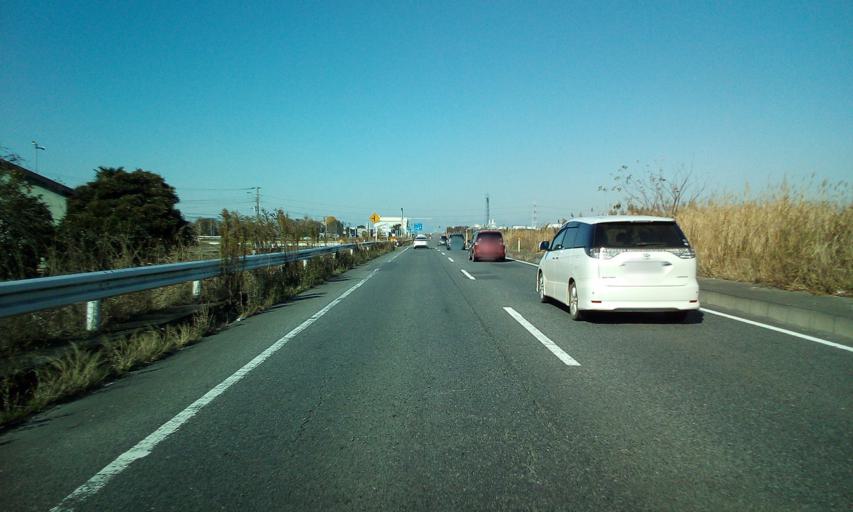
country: JP
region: Ibaraki
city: Sakai
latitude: 36.0724
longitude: 139.7736
